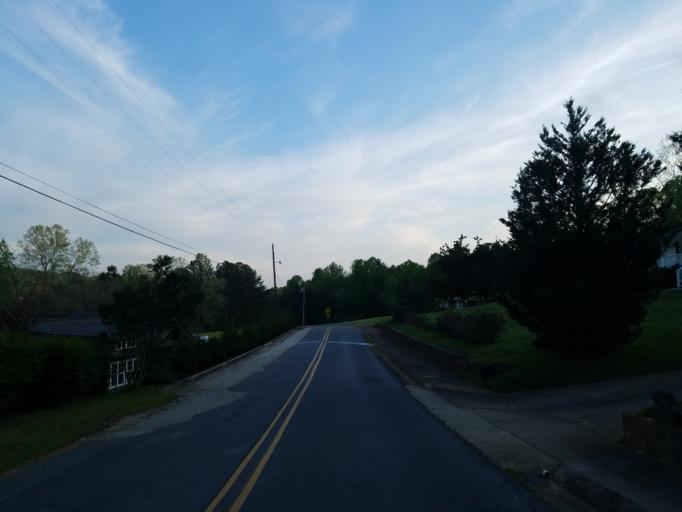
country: US
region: Georgia
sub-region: Fannin County
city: Blue Ridge
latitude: 34.8625
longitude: -84.3293
